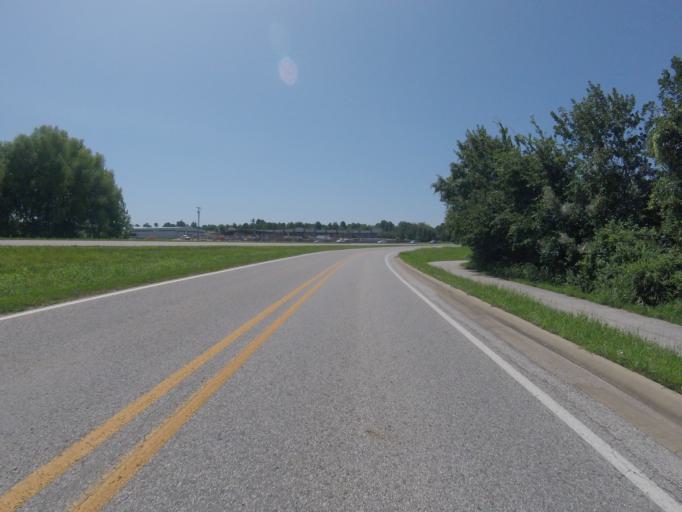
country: US
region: Arkansas
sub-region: Washington County
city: Johnson
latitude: 36.1045
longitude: -94.1827
